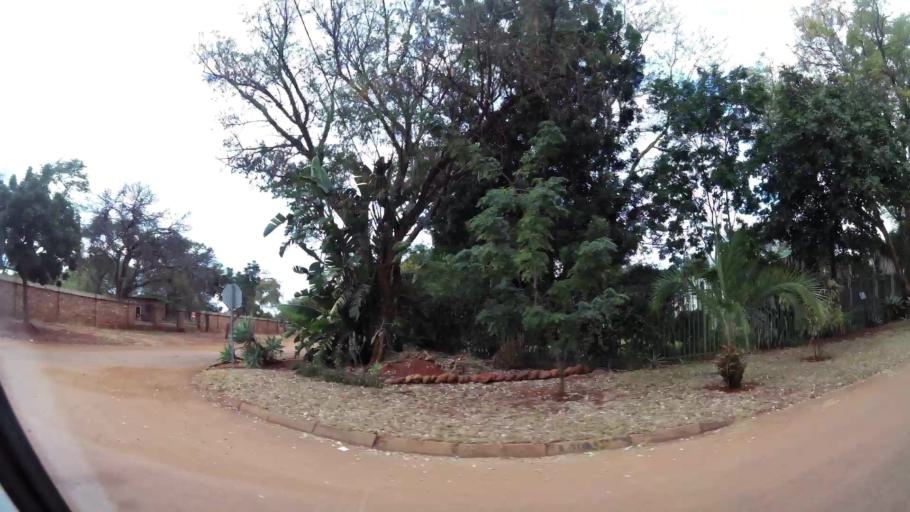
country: ZA
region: Limpopo
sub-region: Waterberg District Municipality
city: Modimolle
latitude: -24.5096
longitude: 28.7183
